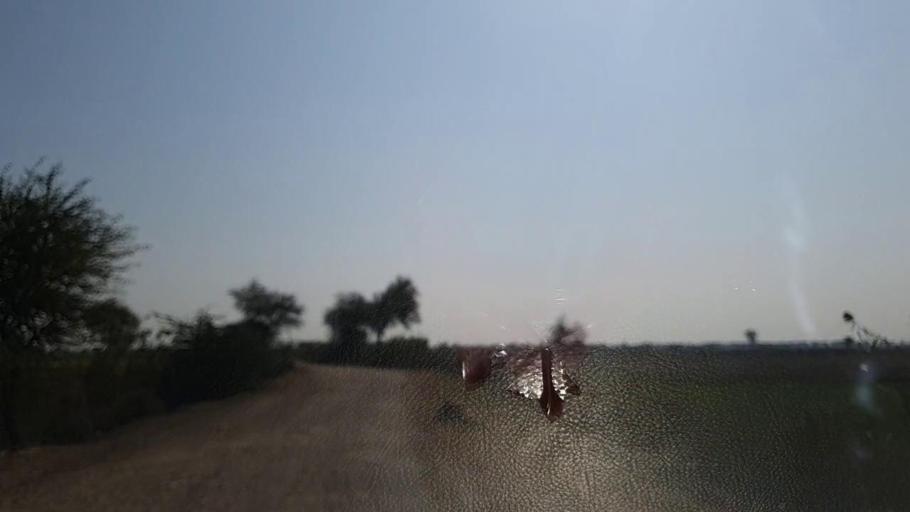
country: PK
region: Sindh
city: Sanghar
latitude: 25.9881
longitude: 69.0610
